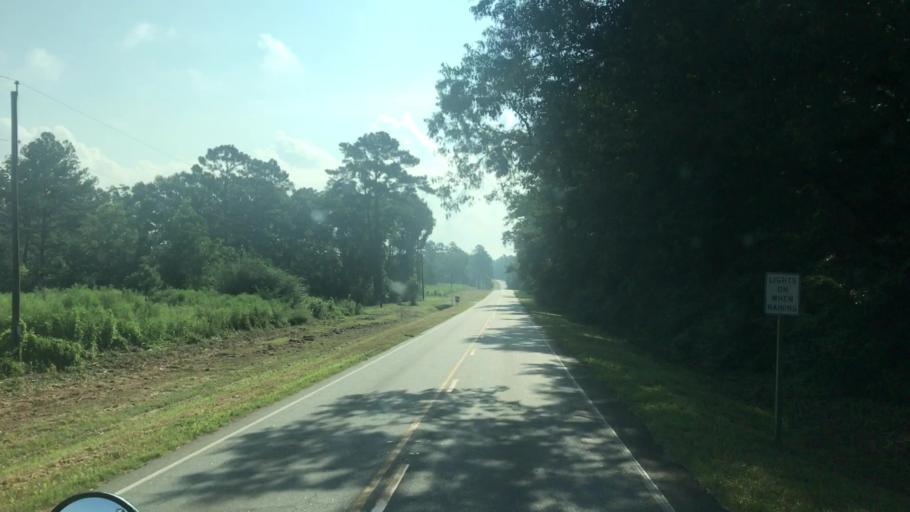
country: US
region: Florida
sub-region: Gadsden County
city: Quincy
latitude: 30.6990
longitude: -84.5301
